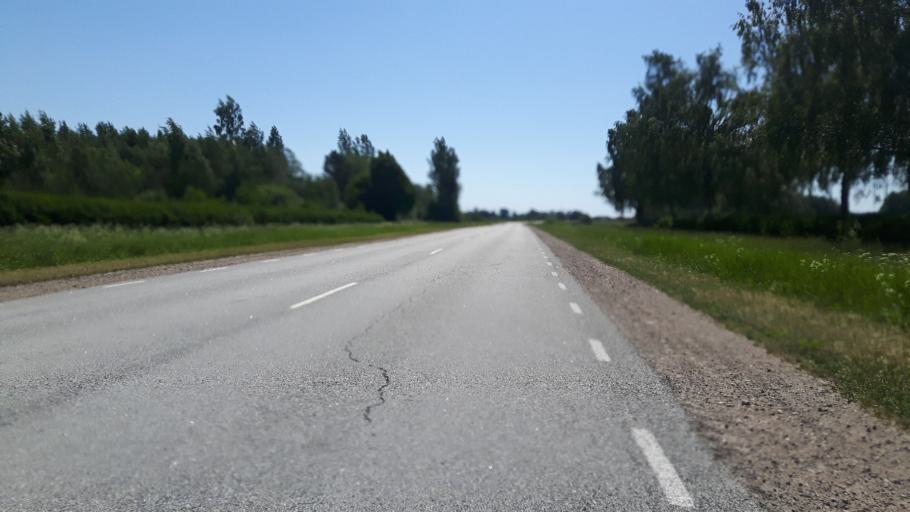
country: EE
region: Paernumaa
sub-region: Tootsi vald
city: Tootsi
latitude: 58.4566
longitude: 24.7790
